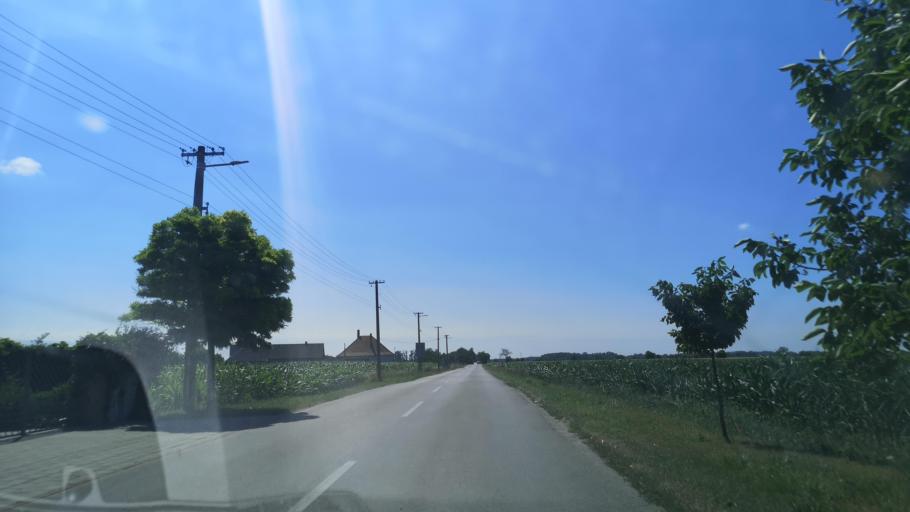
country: SK
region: Bratislavsky
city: Senec
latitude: 48.0991
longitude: 17.4795
